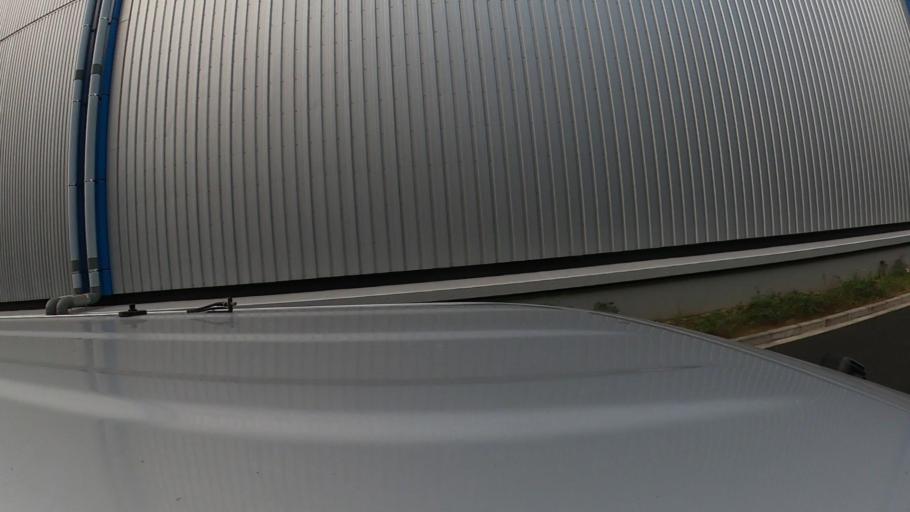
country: JP
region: Kanagawa
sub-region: Kawasaki-shi
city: Kawasaki
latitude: 35.5791
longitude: 139.7506
